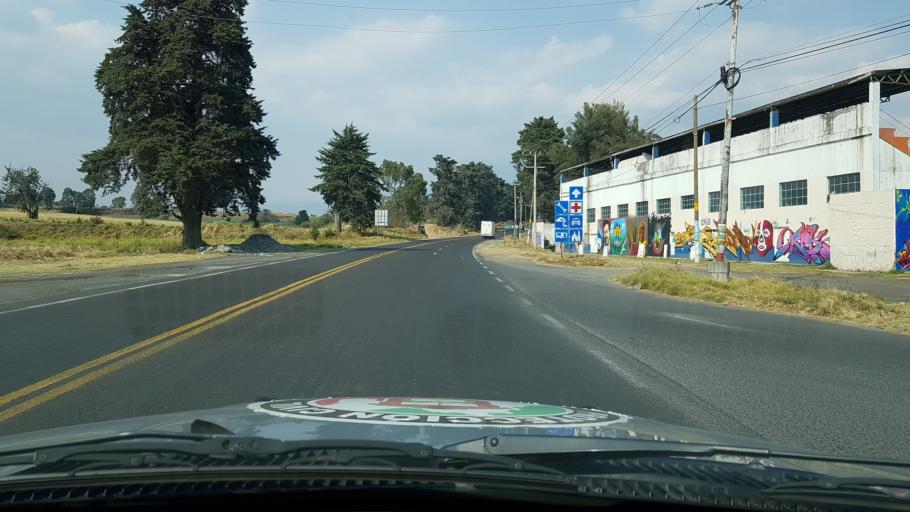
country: MX
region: Mexico
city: Ozumba de Alzate
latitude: 19.0378
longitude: -98.8072
